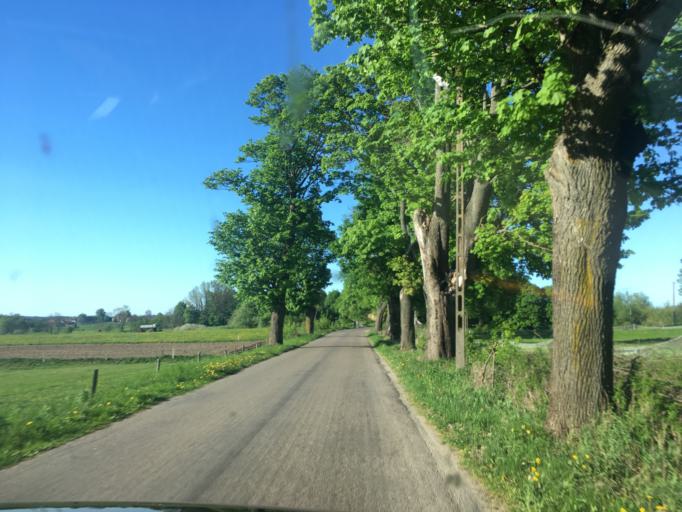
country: PL
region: Warmian-Masurian Voivodeship
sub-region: Powiat piski
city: Ruciane-Nida
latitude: 53.6774
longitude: 21.4938
